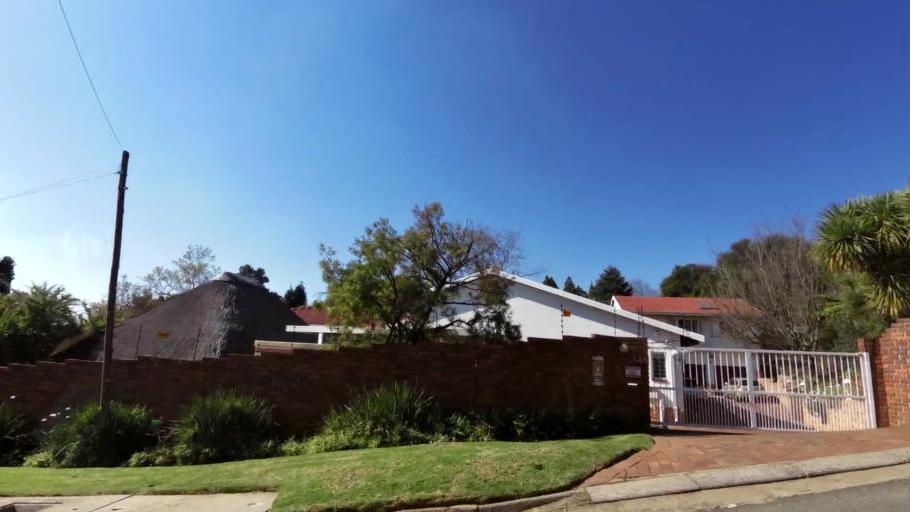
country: ZA
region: Gauteng
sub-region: City of Johannesburg Metropolitan Municipality
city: Roodepoort
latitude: -26.1535
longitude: 27.9400
